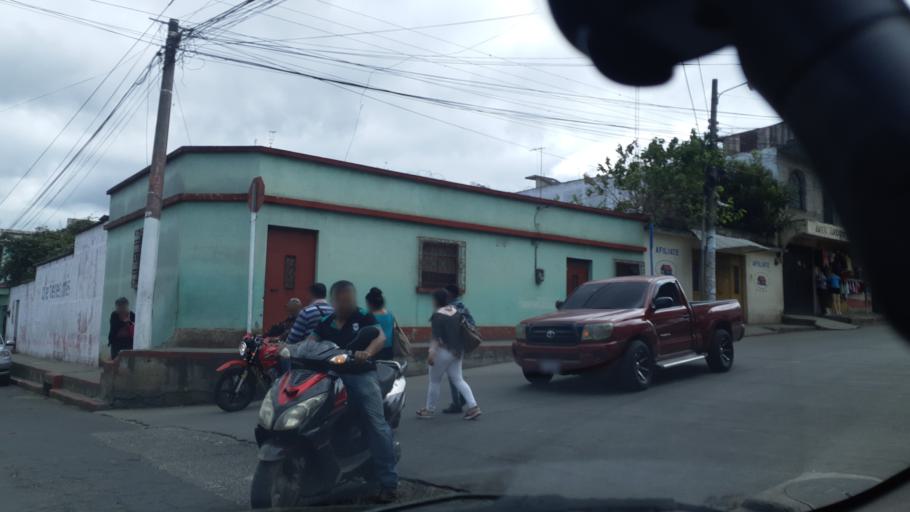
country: GT
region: Chimaltenango
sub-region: Municipio de Chimaltenango
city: Chimaltenango
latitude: 14.6628
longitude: -90.8182
